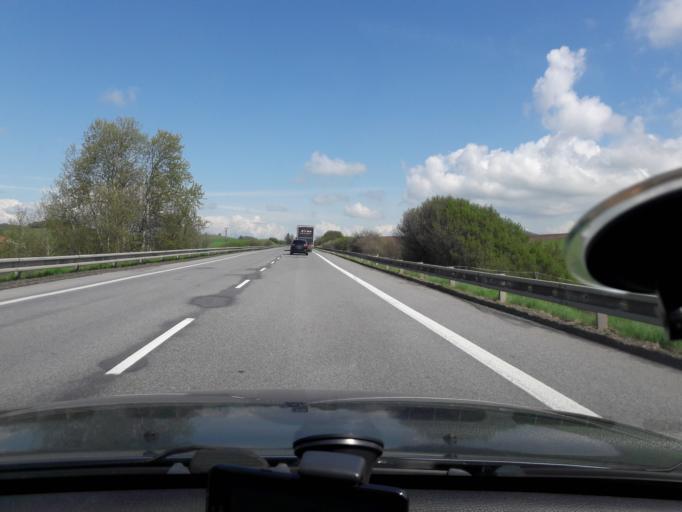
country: SK
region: Banskobystricky
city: Krupina
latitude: 48.4354
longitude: 19.0957
